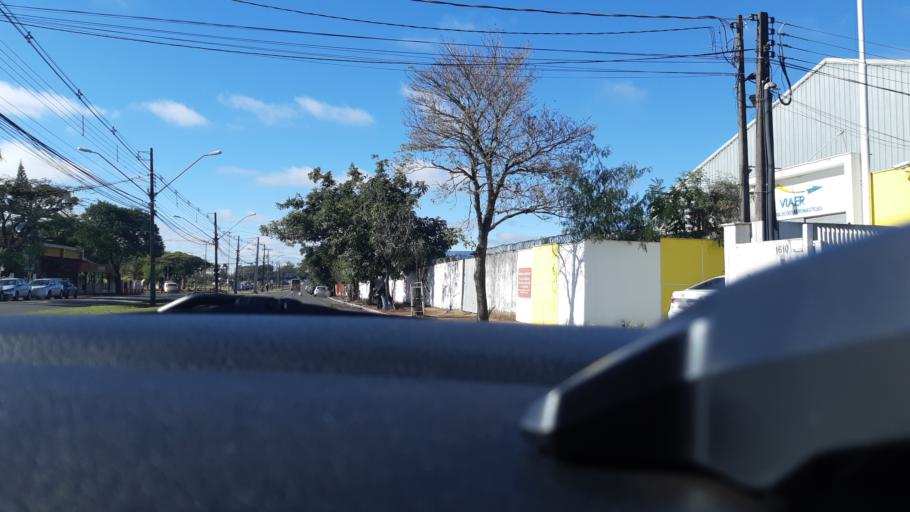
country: BR
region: Parana
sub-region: Londrina
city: Londrina
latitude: -23.3254
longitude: -51.1405
